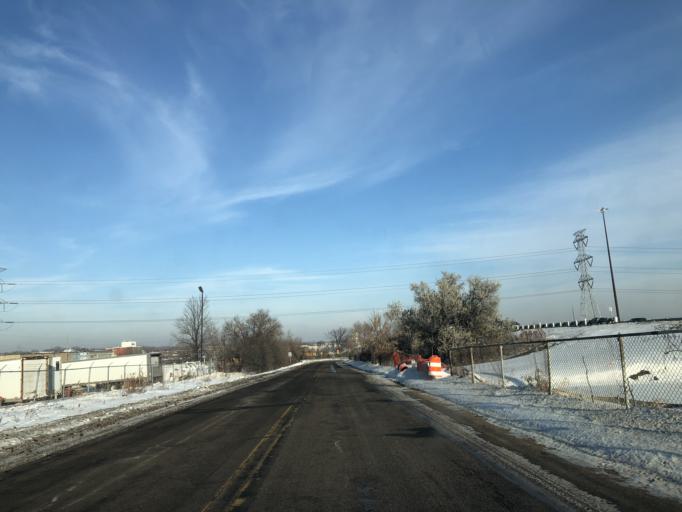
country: US
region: Minnesota
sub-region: Ramsey County
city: Lauderdale
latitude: 45.0179
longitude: -93.1890
